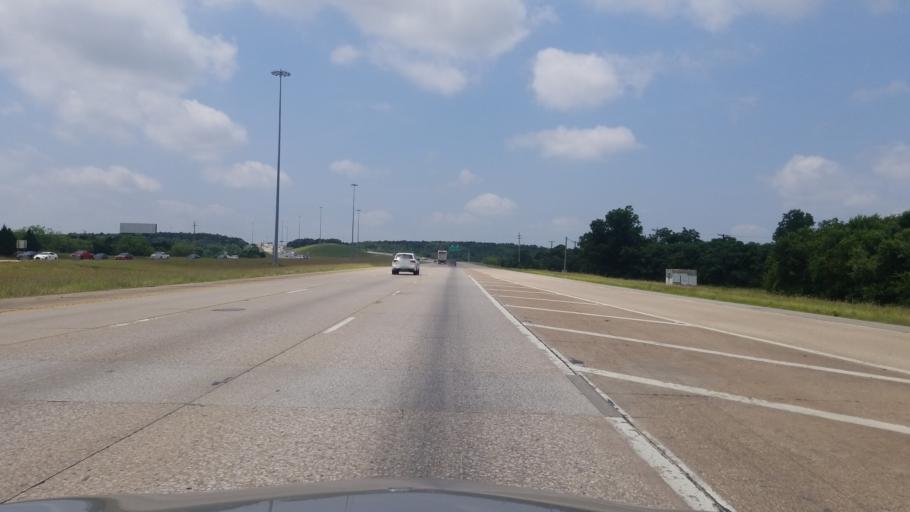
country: US
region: Texas
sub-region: Dallas County
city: Duncanville
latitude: 32.6879
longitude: -96.9414
